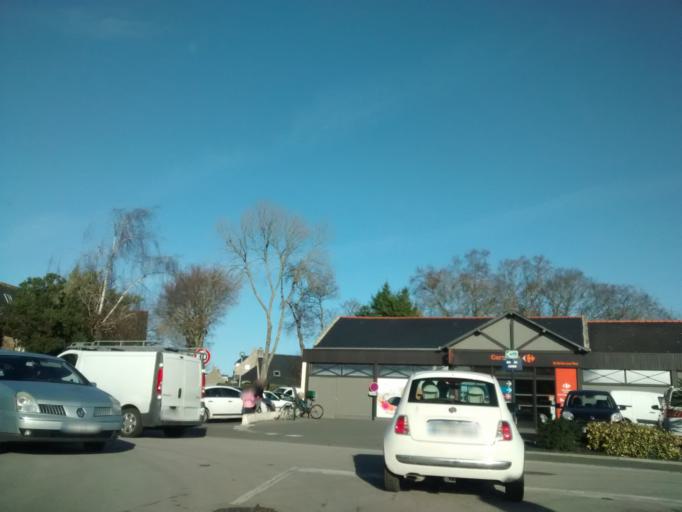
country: FR
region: Brittany
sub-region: Departement d'Ille-et-Vilaine
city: Saint-Briac-sur-Mer
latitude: 48.6183
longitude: -2.1285
